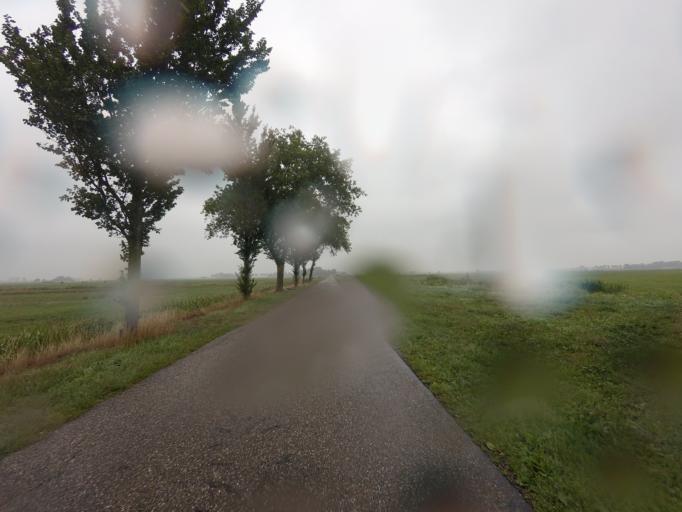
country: NL
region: Friesland
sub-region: Gemeente Boarnsterhim
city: Aldeboarn
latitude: 53.0650
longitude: 5.9184
